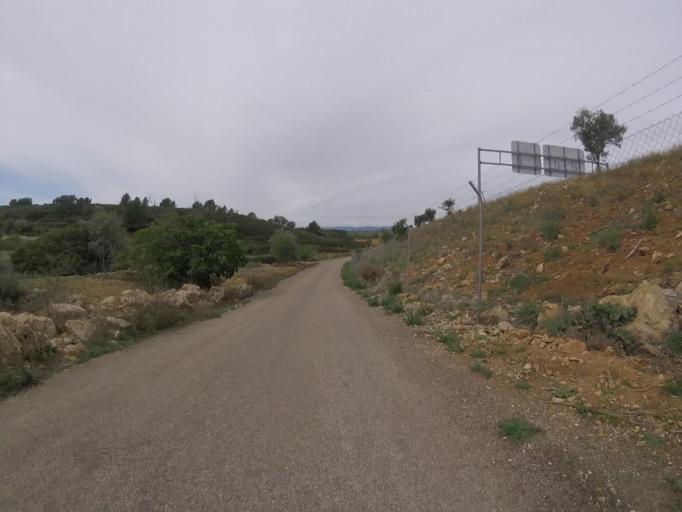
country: ES
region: Valencia
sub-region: Provincia de Castello
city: Benlloch
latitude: 40.1971
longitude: 0.0617
